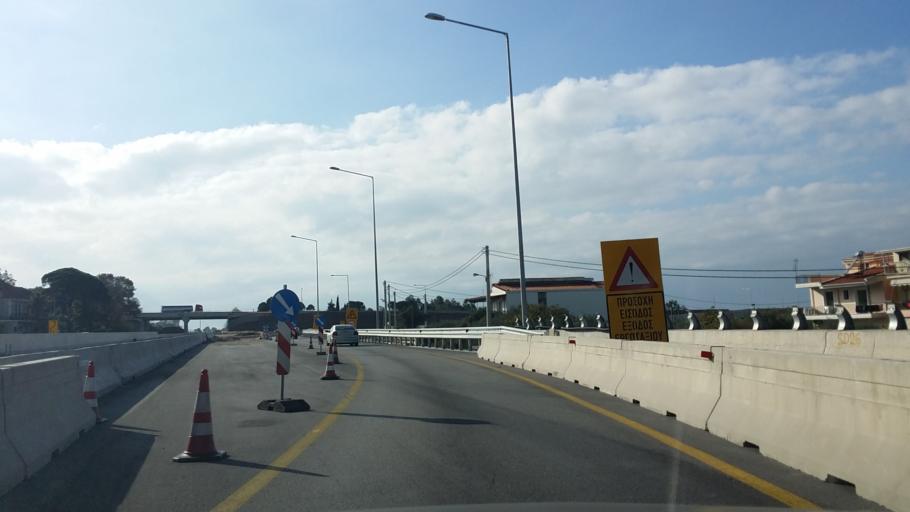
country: GR
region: West Greece
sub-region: Nomos Achaias
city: Rio
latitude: 38.3003
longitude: 21.7958
